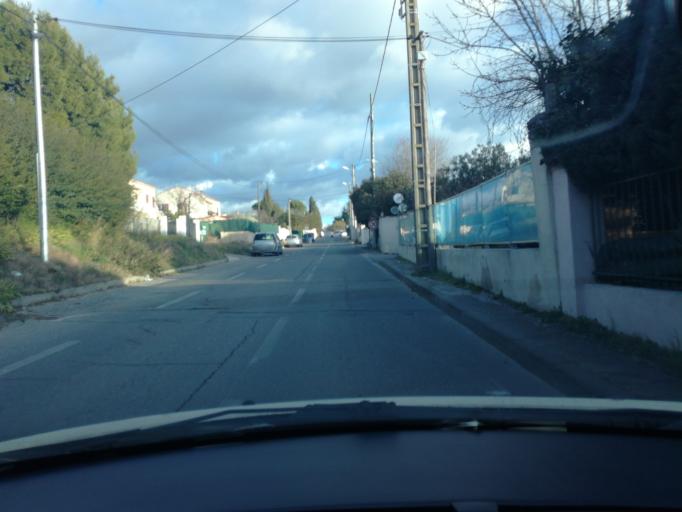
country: FR
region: Provence-Alpes-Cote d'Azur
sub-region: Departement des Bouches-du-Rhone
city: Allauch
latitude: 43.3304
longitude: 5.4704
